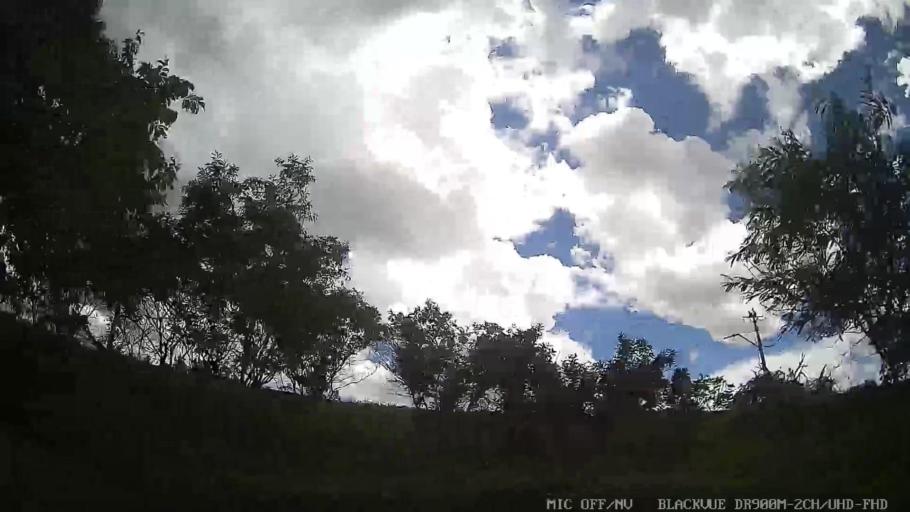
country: BR
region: Sao Paulo
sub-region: Jaguariuna
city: Jaguariuna
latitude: -22.6927
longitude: -47.0085
